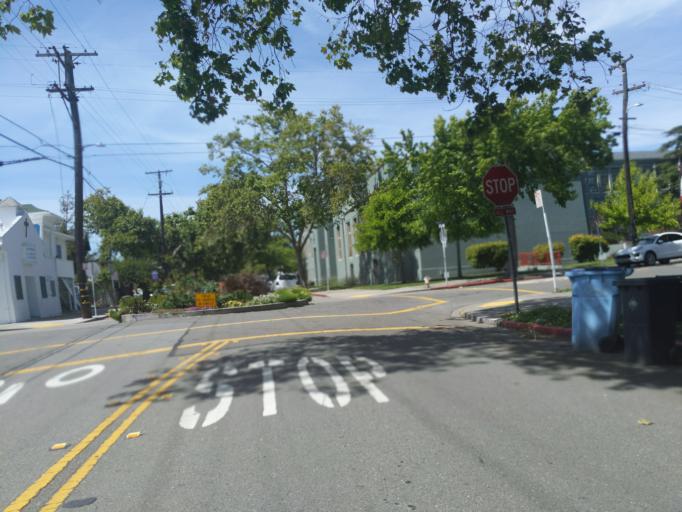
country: US
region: California
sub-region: Alameda County
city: Berkeley
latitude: 37.8519
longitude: -122.2740
